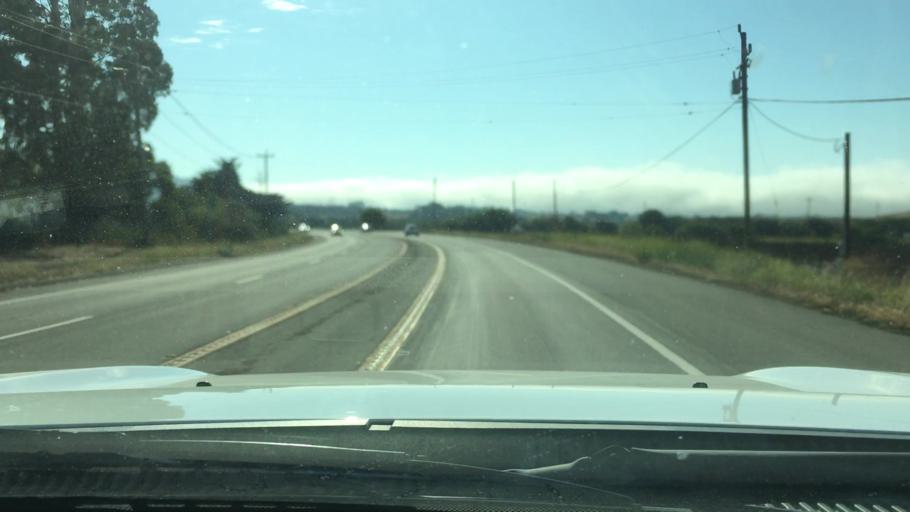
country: US
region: California
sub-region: San Luis Obispo County
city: Los Osos
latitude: 35.2998
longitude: -120.7745
